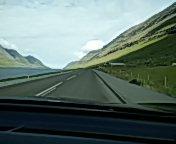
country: FO
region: Nordoyar
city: Klaksvik
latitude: 62.3016
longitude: -6.5227
